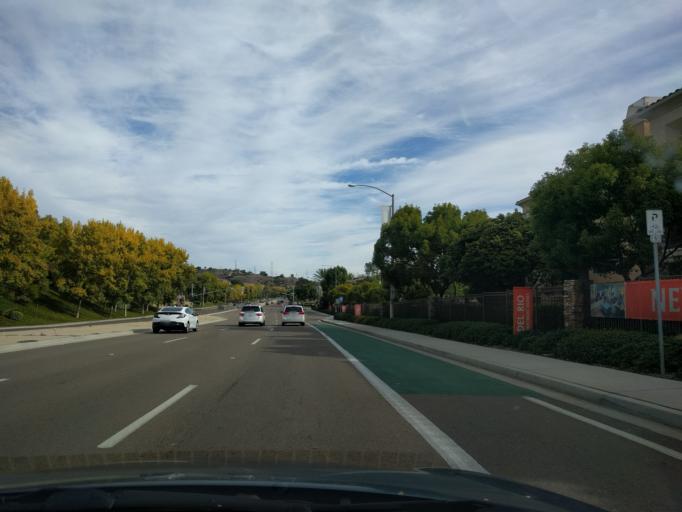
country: US
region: California
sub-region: San Diego County
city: San Diego
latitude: 32.7799
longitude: -117.1330
